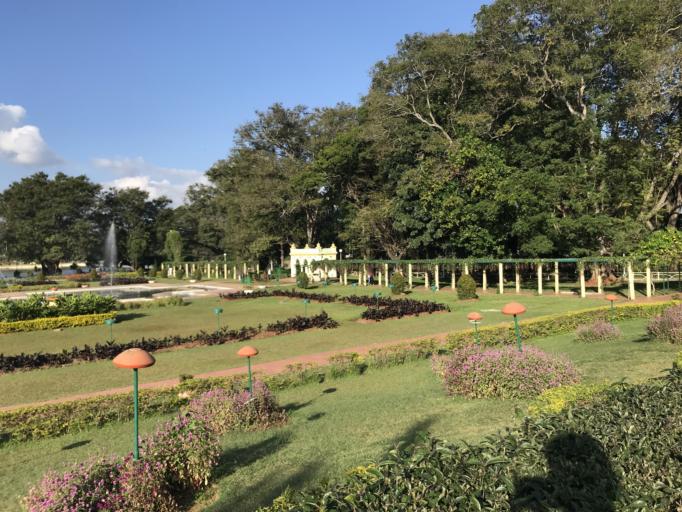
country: IN
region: Karnataka
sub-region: Mandya
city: Shrirangapattana
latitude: 12.4223
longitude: 76.5733
